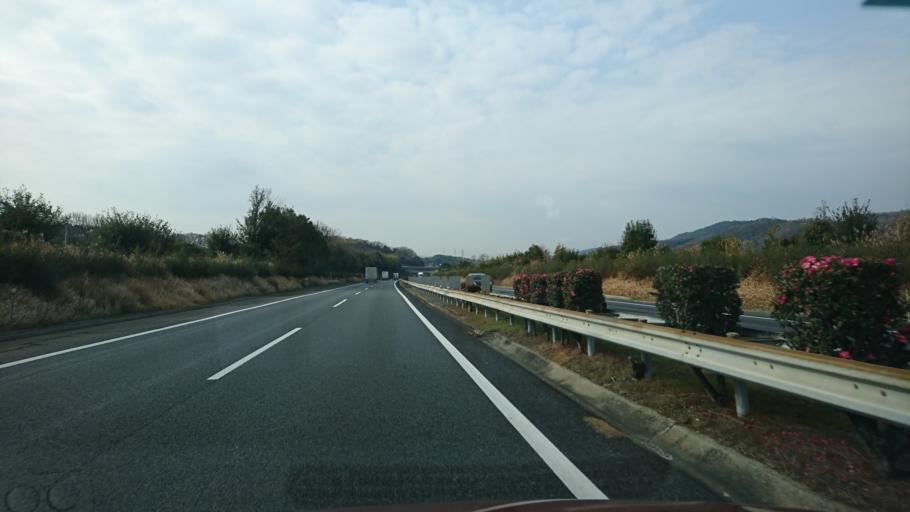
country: JP
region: Hiroshima
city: Kannabecho-yahiro
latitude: 34.5322
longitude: 133.4523
